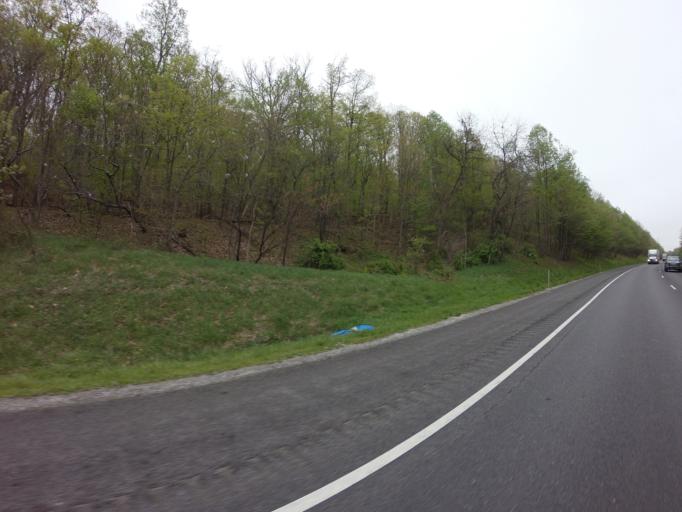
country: US
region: Maryland
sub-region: Washington County
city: Boonsboro
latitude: 39.5527
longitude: -77.6092
